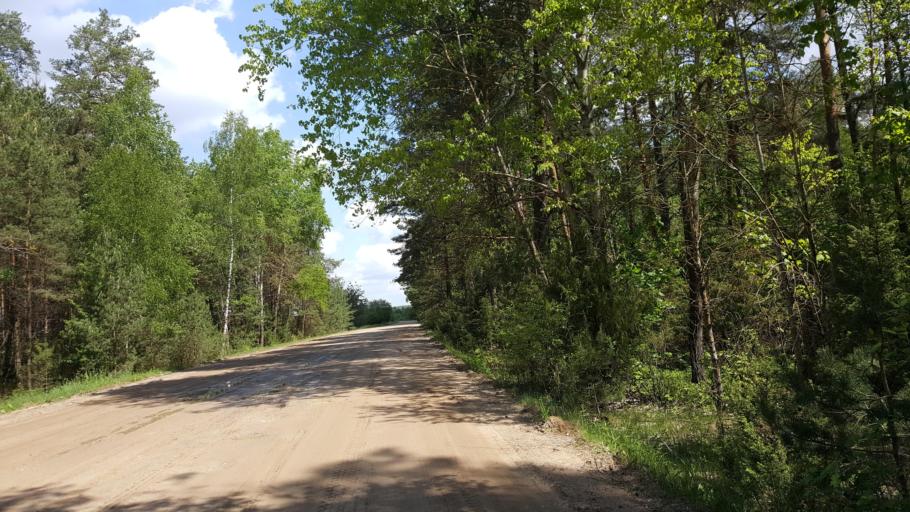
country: BY
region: Brest
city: Kamyanyets
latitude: 52.4390
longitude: 23.9750
